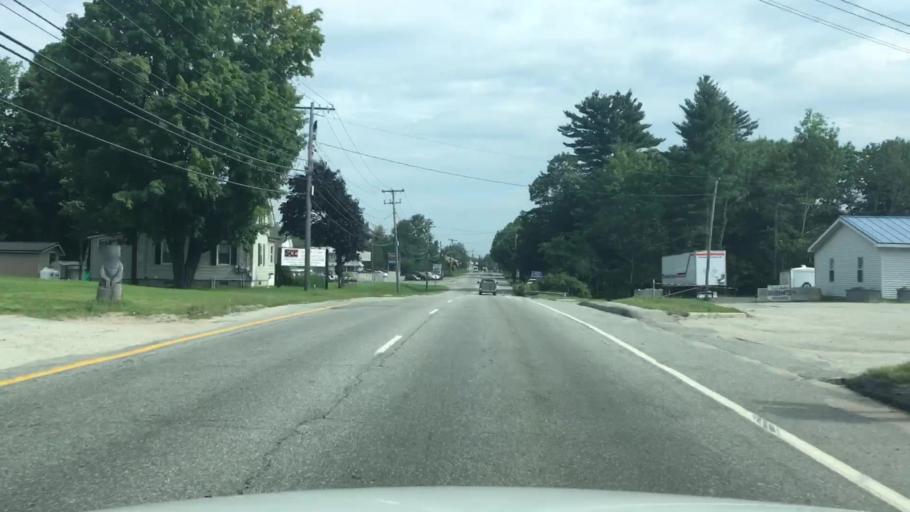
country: US
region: Maine
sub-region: Androscoggin County
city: Auburn
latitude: 44.0691
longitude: -70.2457
